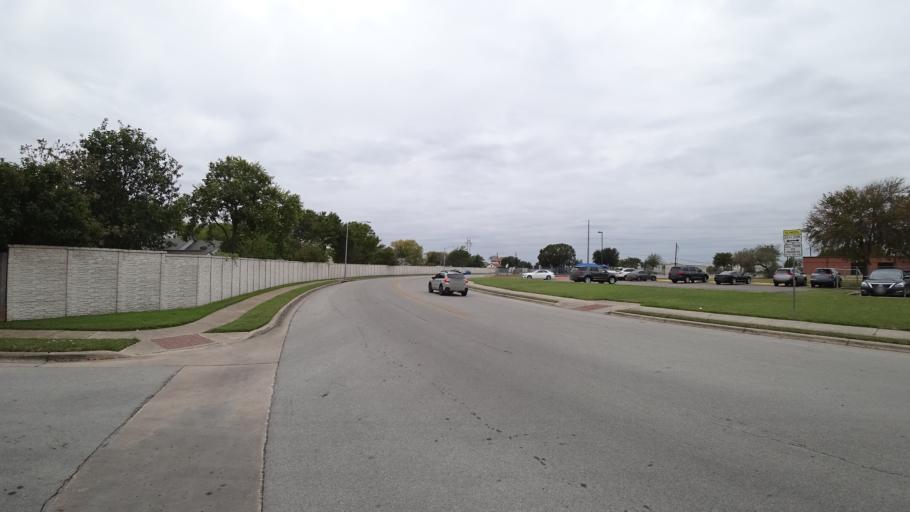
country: US
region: Texas
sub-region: Travis County
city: Wells Branch
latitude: 30.4441
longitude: -97.6859
